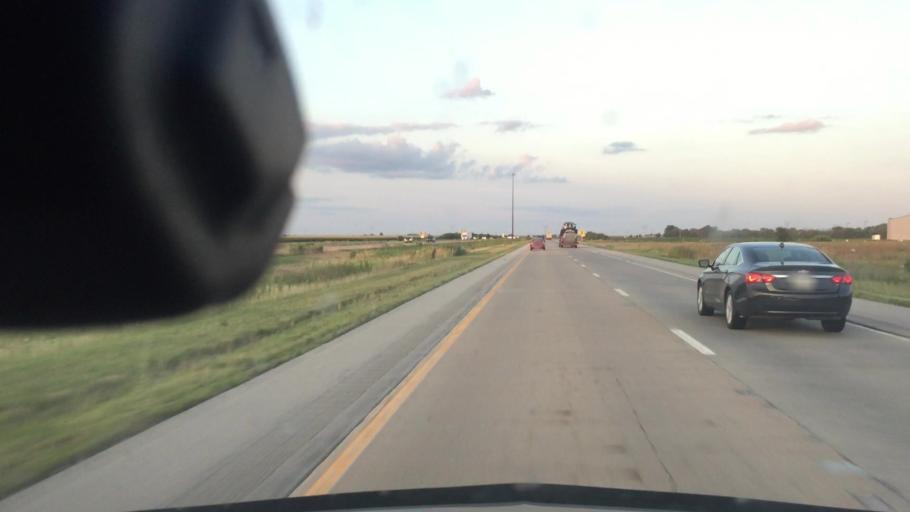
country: US
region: Illinois
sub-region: Livingston County
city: Dwight
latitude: 41.1173
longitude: -88.4132
